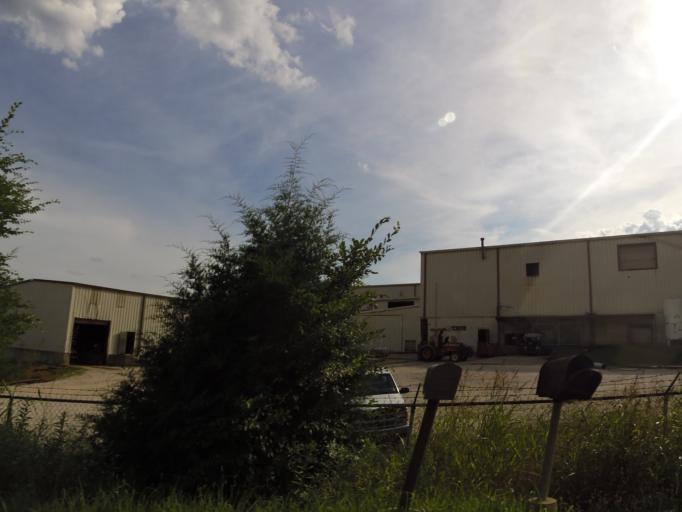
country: US
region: Tennessee
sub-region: Benton County
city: Camden
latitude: 36.0197
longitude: -88.0603
